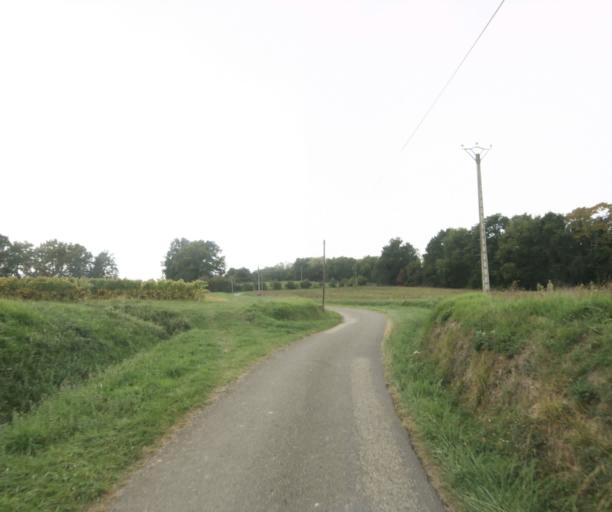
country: FR
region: Midi-Pyrenees
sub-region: Departement du Gers
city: Eauze
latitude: 43.8850
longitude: 0.1115
